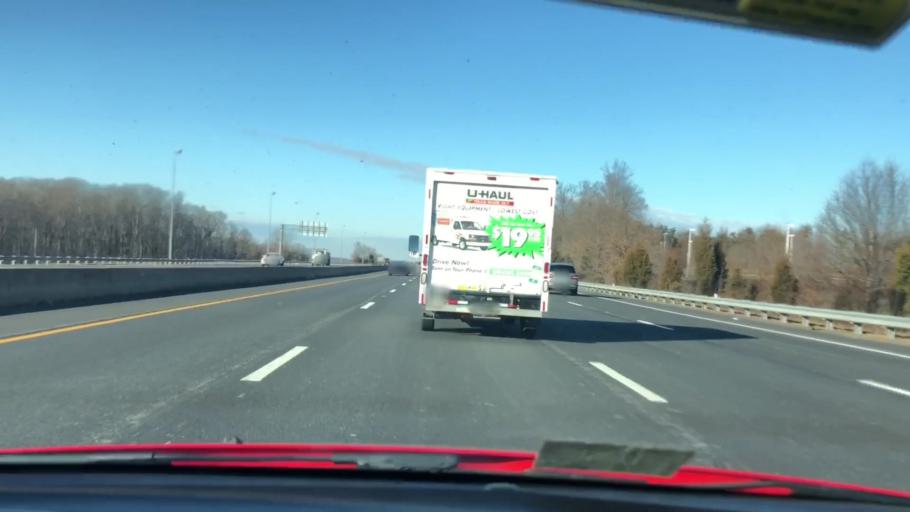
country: US
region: Virginia
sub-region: Loudoun County
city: Dulles Town Center
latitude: 39.0348
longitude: -77.4312
